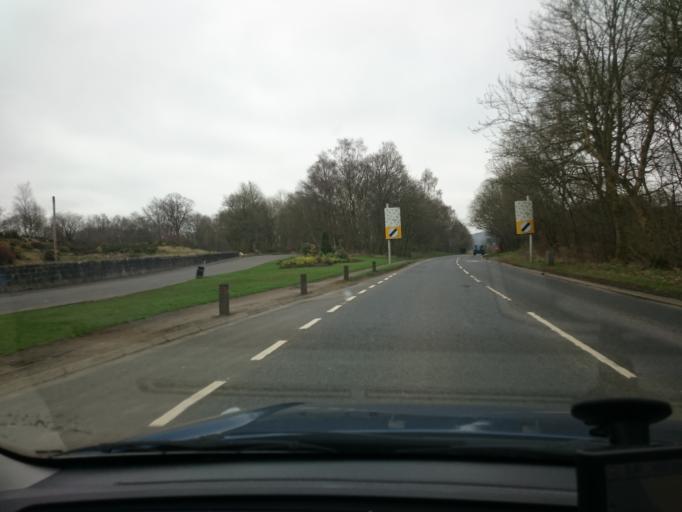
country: GB
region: Scotland
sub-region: North Lanarkshire
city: Kilsyth
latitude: 55.9795
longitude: -4.0327
